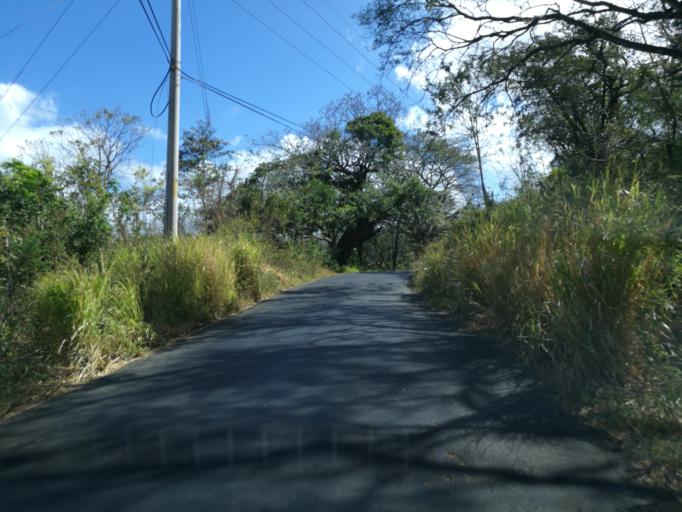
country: CR
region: Guanacaste
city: Liberia
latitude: 10.7289
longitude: -85.3920
